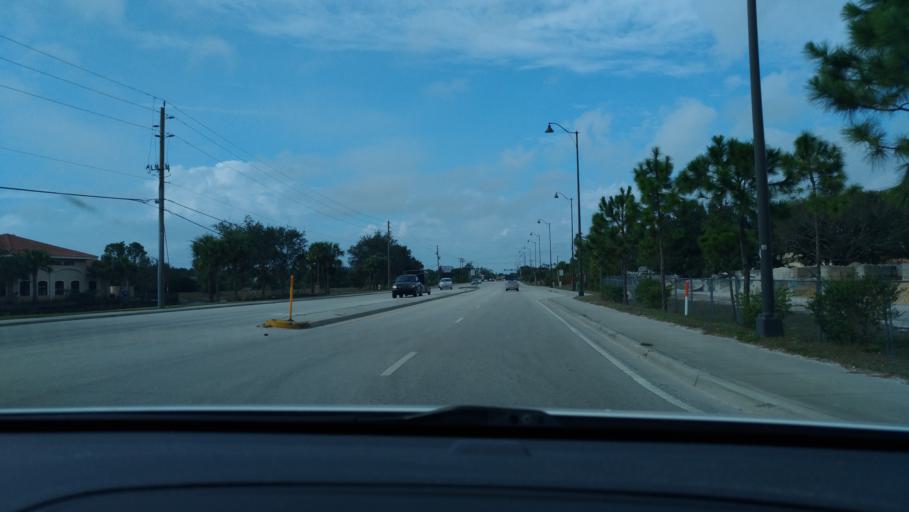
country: US
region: Florida
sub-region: Lee County
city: Bonita Springs
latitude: 26.3734
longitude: -81.8016
